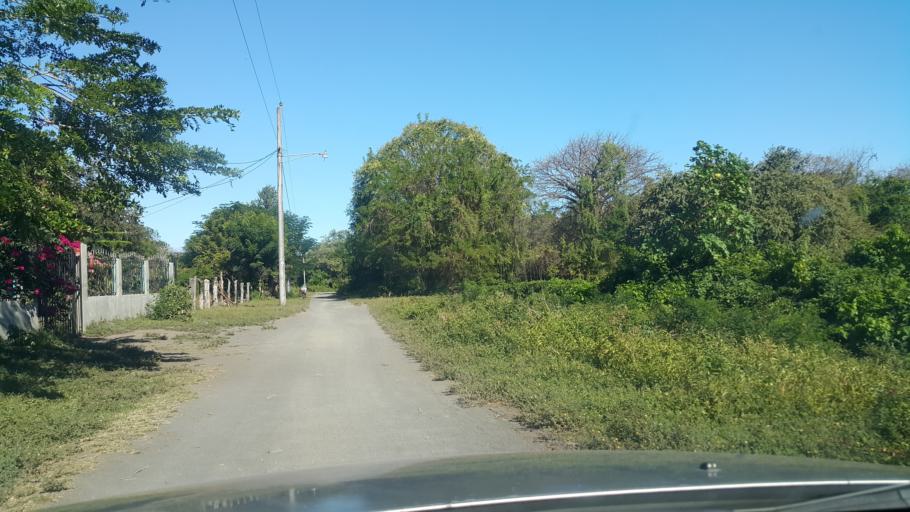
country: NI
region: Rivas
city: Altagracia
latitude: 11.4909
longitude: -85.6040
